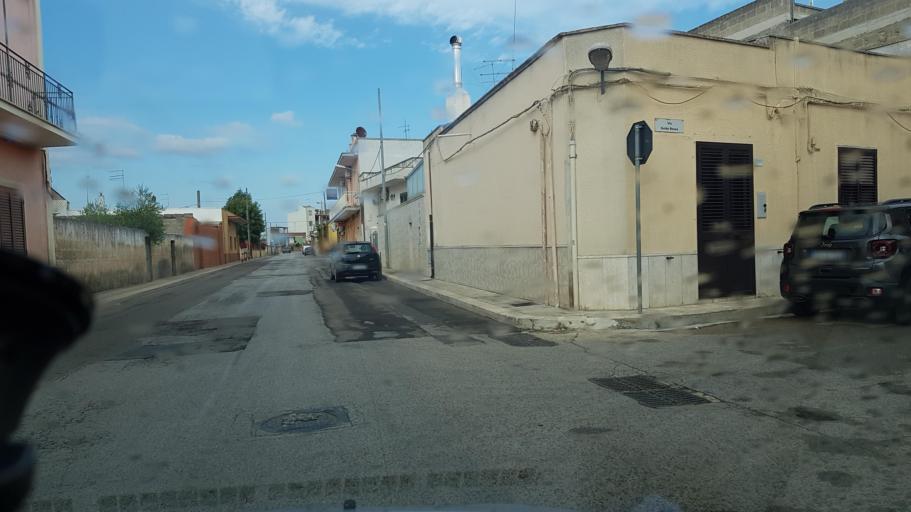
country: IT
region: Apulia
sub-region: Provincia di Brindisi
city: Torre Santa Susanna
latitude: 40.4678
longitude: 17.7350
